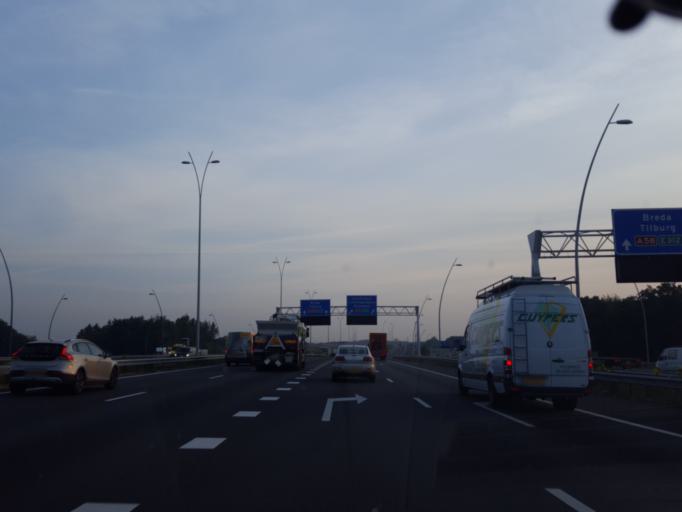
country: NL
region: North Brabant
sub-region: Gemeente Eindhoven
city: Meerhoven
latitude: 51.4685
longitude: 5.4064
